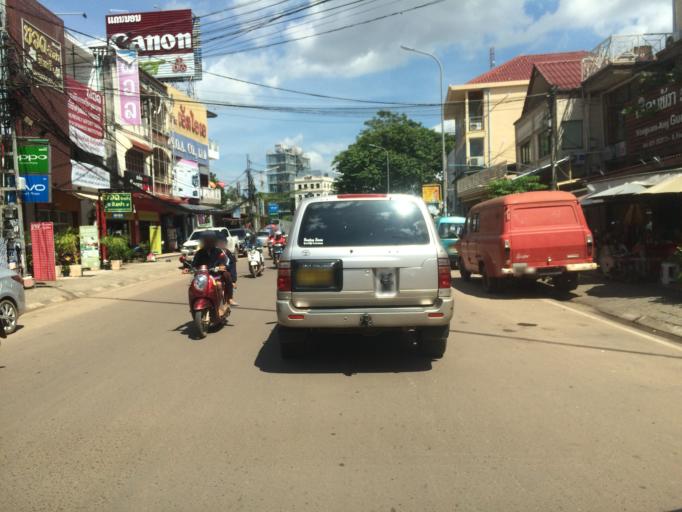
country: LA
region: Vientiane
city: Vientiane
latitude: 17.9685
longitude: 102.6144
